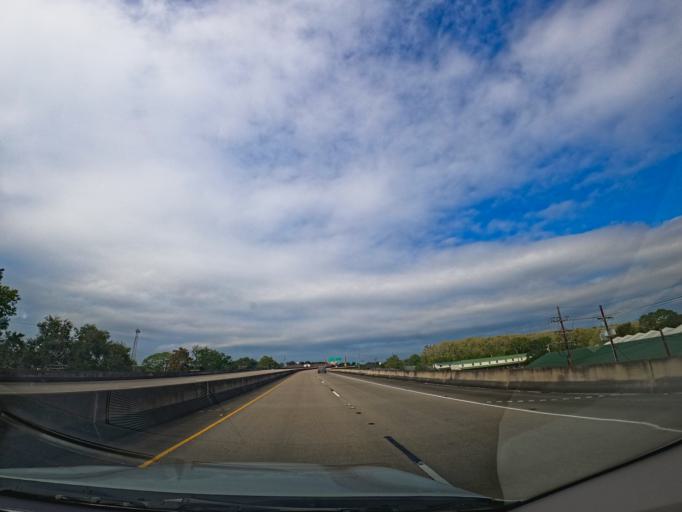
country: US
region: Louisiana
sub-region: Saint Mary Parish
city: Morgan City
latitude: 29.6966
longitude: -91.1768
